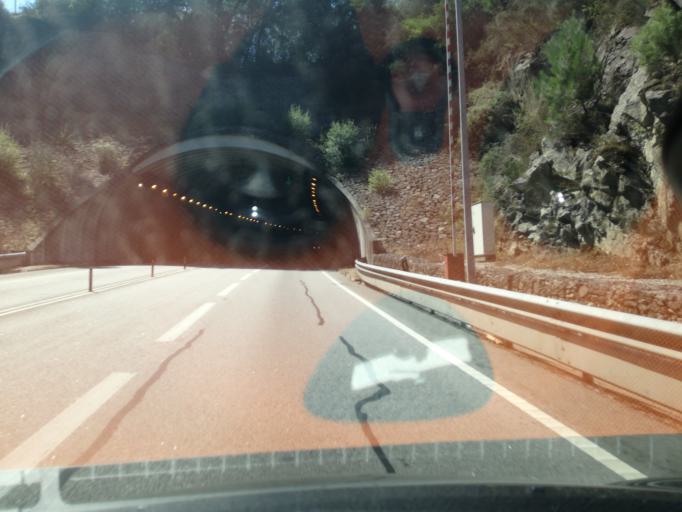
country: PT
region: Viana do Castelo
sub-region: Vila Nova de Cerveira
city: Vila Nova de Cerveira
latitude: 41.9099
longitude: -8.7836
